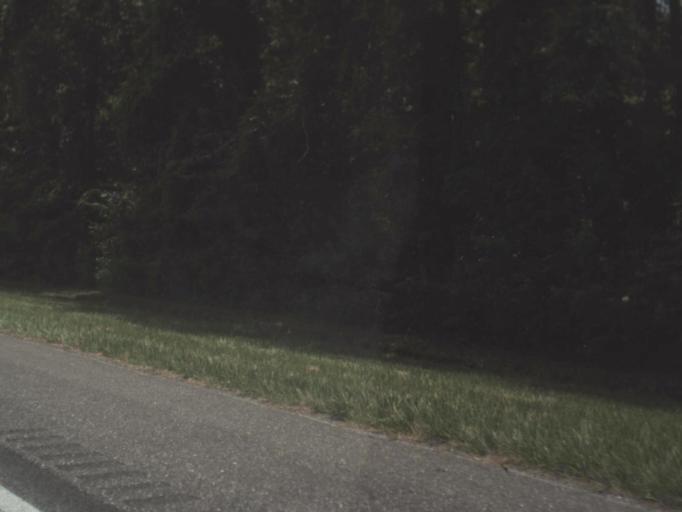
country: US
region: Florida
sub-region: Jefferson County
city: Monticello
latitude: 30.4451
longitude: -83.7150
